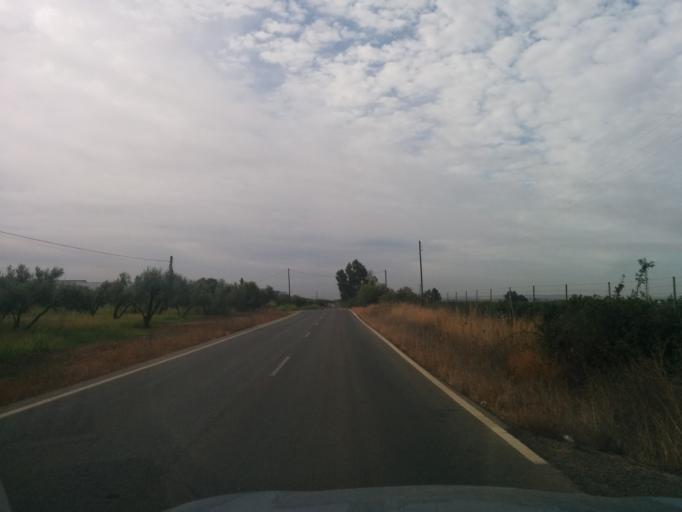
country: ES
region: Andalusia
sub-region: Provincia de Sevilla
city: Guillena
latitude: 37.5435
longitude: -6.0360
